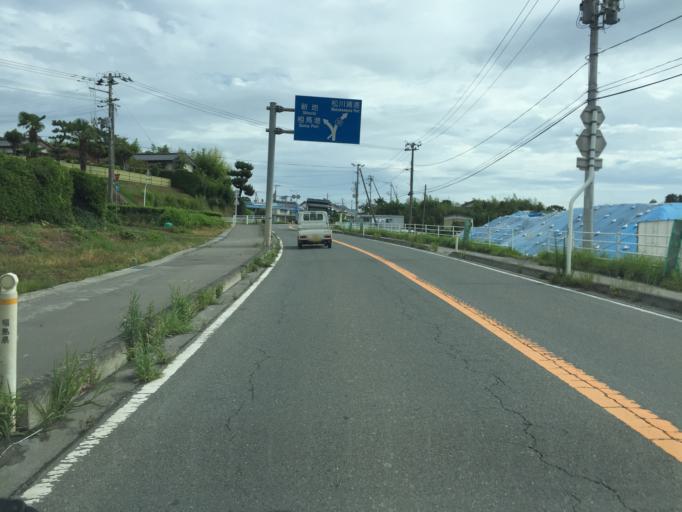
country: JP
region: Miyagi
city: Marumori
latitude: 37.8213
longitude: 140.9473
